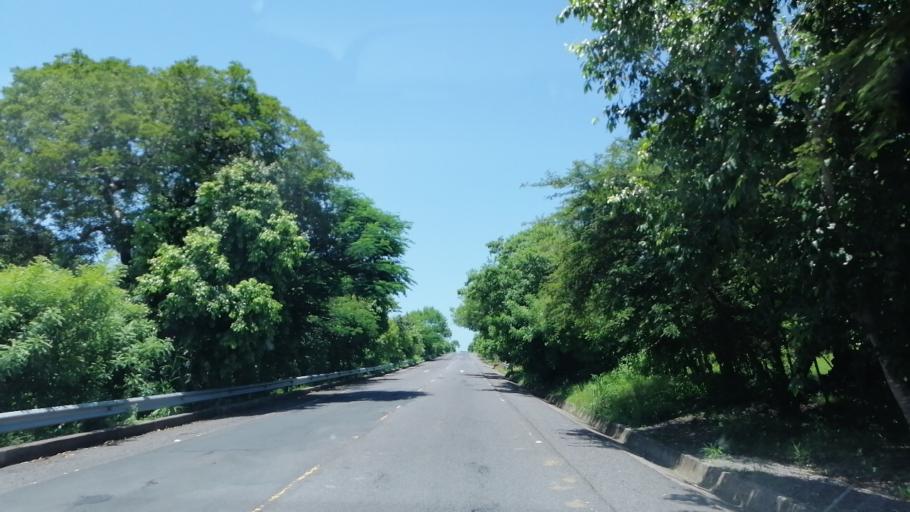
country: SV
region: Chalatenango
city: Chalatenango
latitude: 14.0306
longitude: -88.9513
